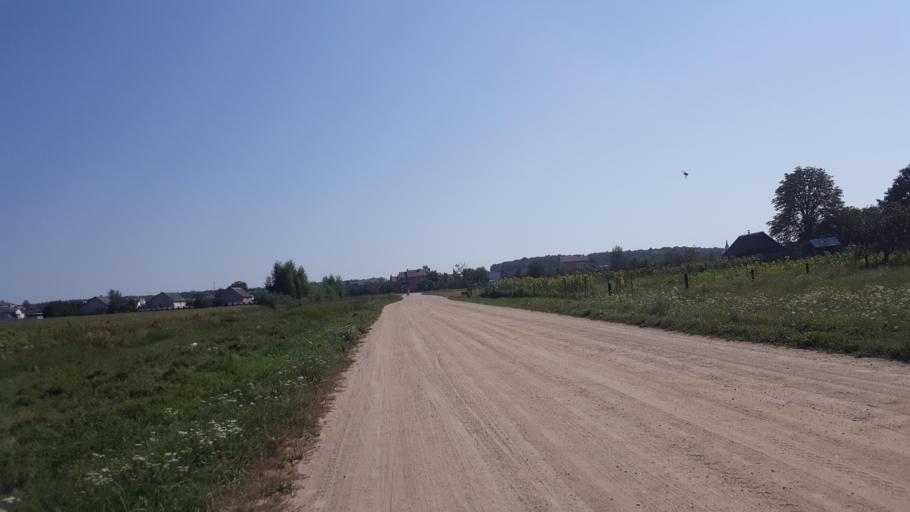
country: BY
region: Brest
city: Vysokaye
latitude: 52.4038
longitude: 23.4501
